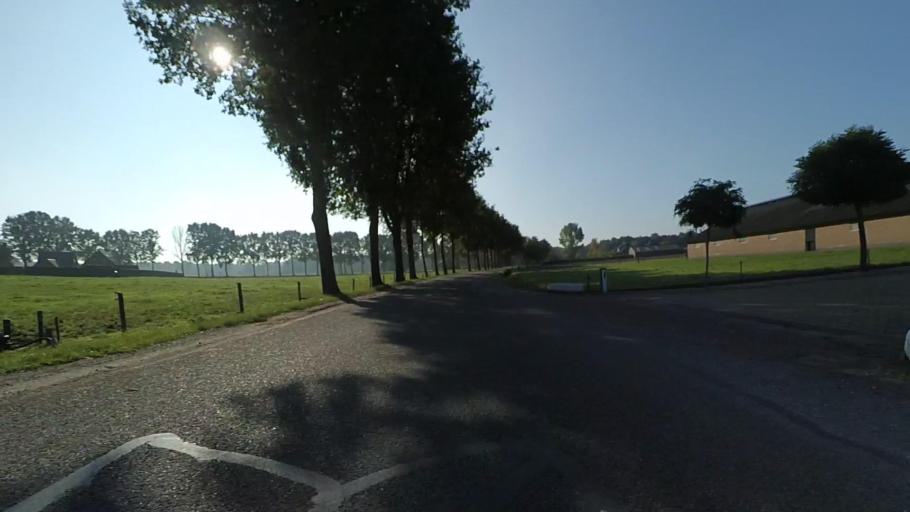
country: NL
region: Gelderland
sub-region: Gemeente Putten
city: Putten
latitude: 52.2388
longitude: 5.5542
